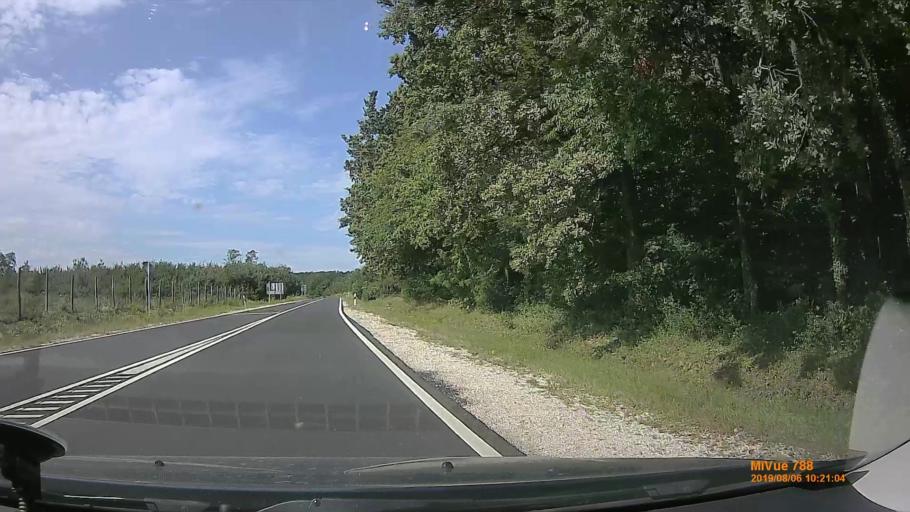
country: HU
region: Somogy
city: Balatonbereny
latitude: 46.6784
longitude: 17.3378
